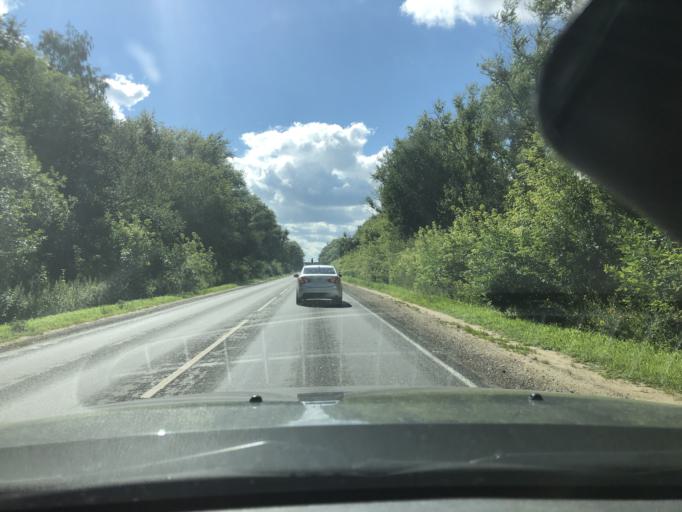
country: RU
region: Tula
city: Severo-Zadonsk
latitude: 53.9700
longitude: 38.4051
